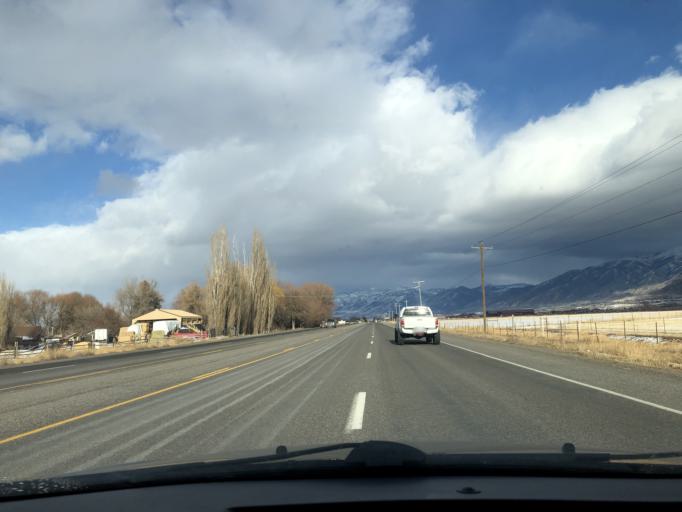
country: US
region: Utah
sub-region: Cache County
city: Wellsville
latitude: 41.6574
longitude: -111.9012
